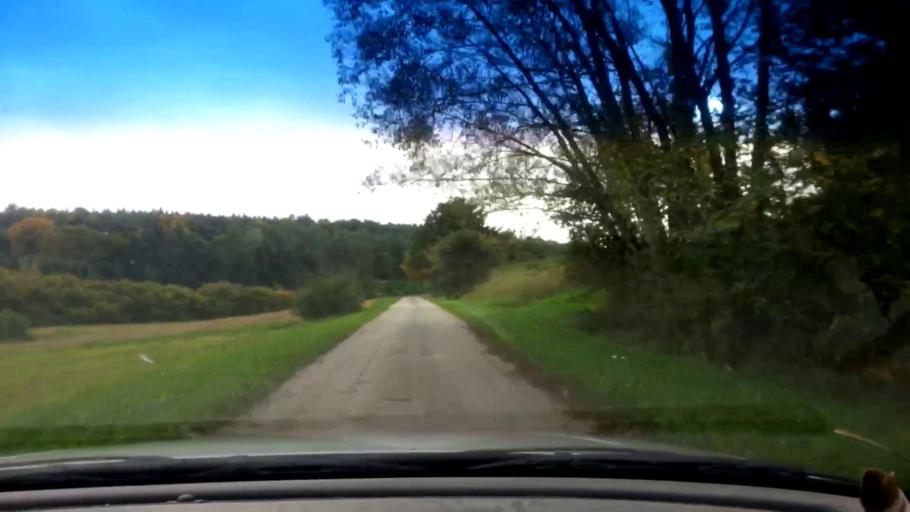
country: DE
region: Bavaria
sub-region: Upper Franconia
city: Priesendorf
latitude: 49.8941
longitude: 10.7075
